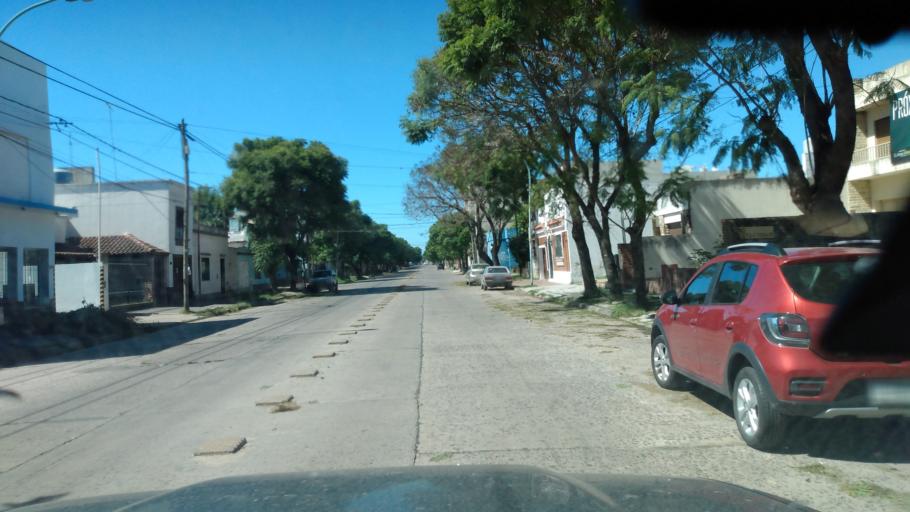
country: AR
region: Buenos Aires
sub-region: Partido de Lujan
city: Lujan
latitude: -34.5691
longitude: -59.1206
